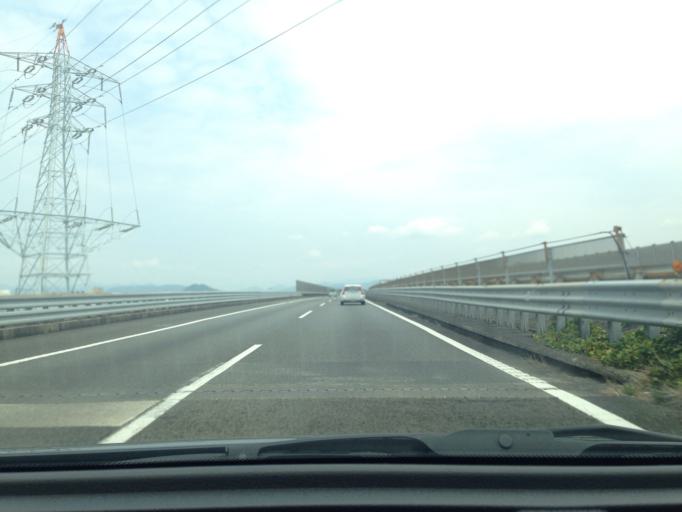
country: JP
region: Shizuoka
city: Fujieda
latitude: 34.8511
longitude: 138.2820
